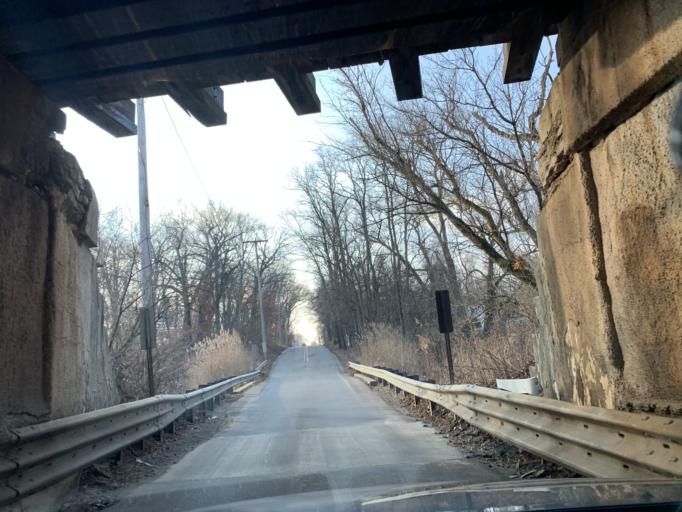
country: US
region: Indiana
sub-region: Porter County
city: Portage
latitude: 41.5817
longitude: -87.1535
